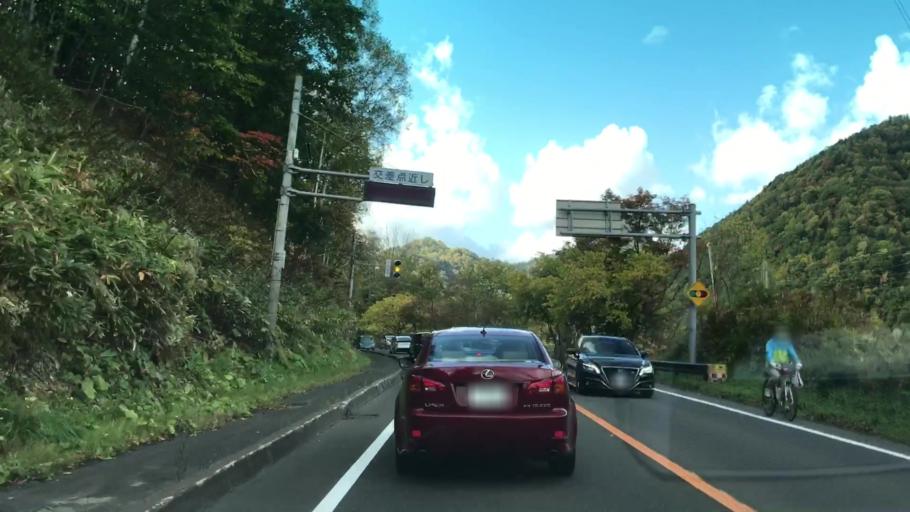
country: JP
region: Hokkaido
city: Sapporo
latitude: 42.9701
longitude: 141.1773
